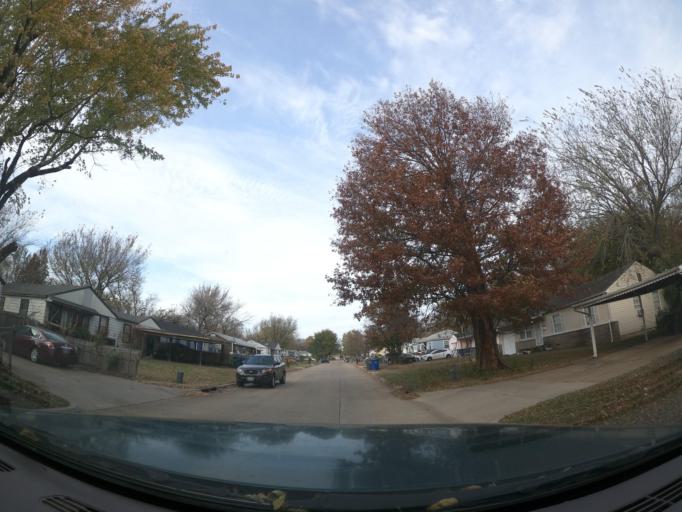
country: US
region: Oklahoma
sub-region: Tulsa County
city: Turley
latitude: 36.2214
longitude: -95.9951
